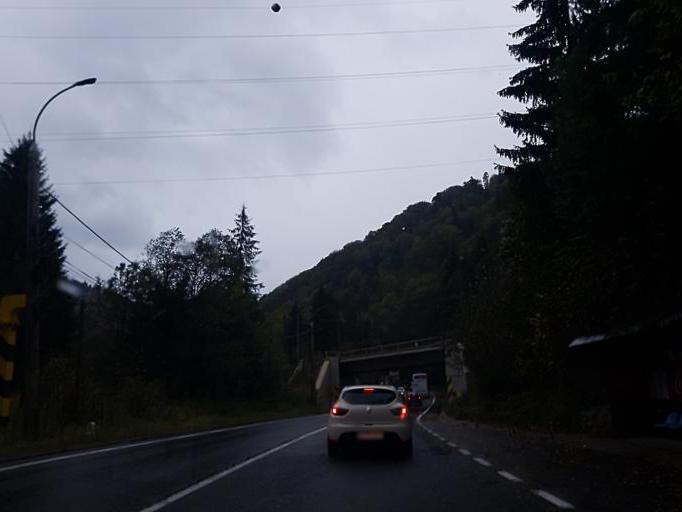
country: RO
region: Prahova
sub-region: Oras Azuga
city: Azuga
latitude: 45.4293
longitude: 25.5543
